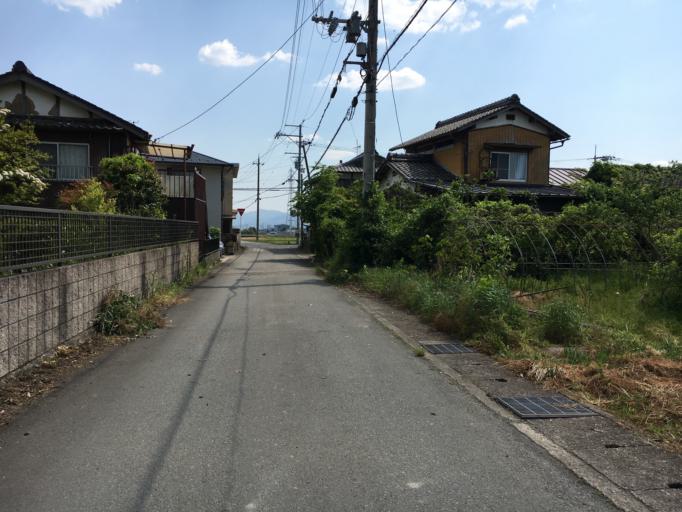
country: JP
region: Kyoto
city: Kameoka
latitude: 35.0792
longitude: 135.5562
